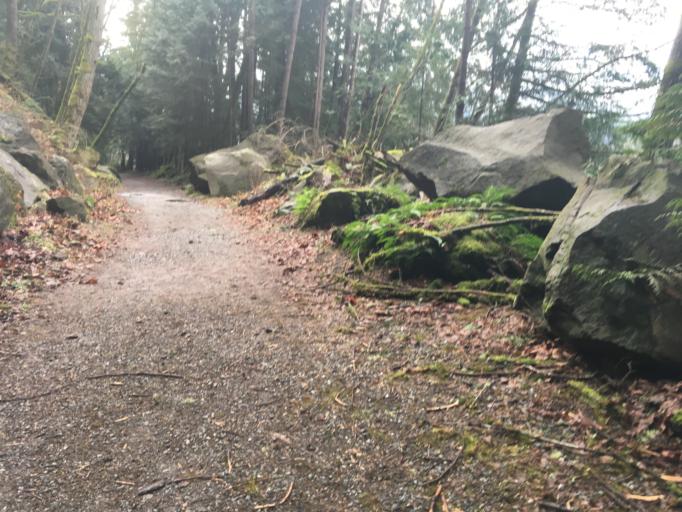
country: US
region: Washington
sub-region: Whatcom County
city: Sudden Valley
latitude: 48.7137
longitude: -122.2976
